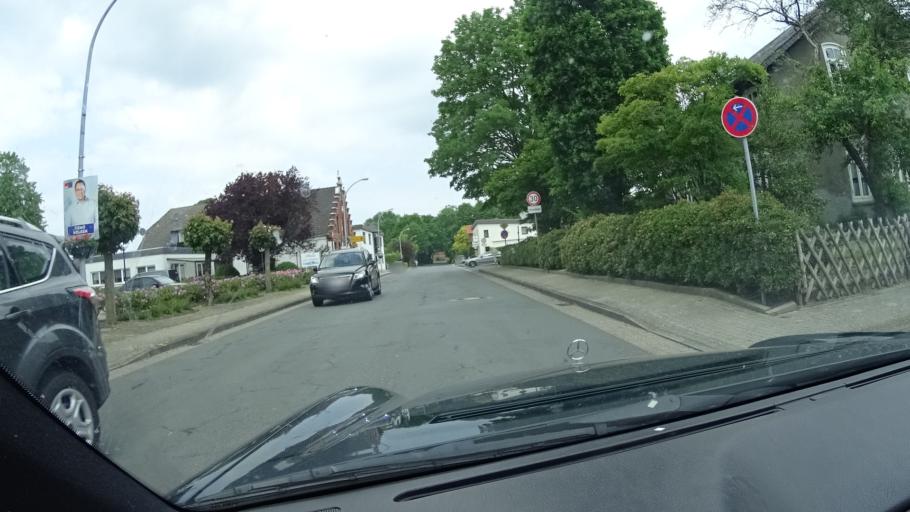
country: DE
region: Lower Saxony
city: Butjadingen
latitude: 53.5912
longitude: 8.2777
